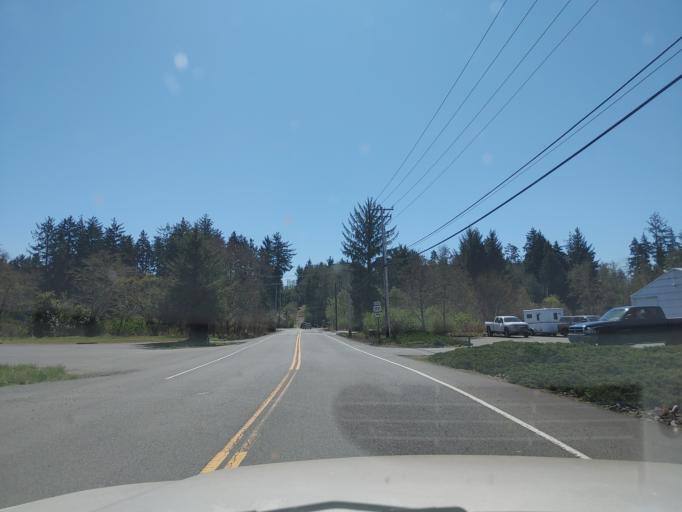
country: US
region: Oregon
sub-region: Clatsop County
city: Warrenton
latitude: 46.1552
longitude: -123.9050
